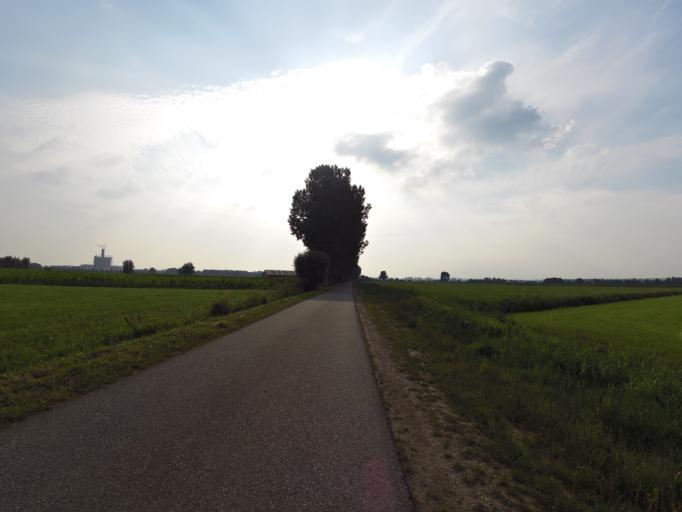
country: NL
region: Gelderland
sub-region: Gemeente Rheden
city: Rheden
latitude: 51.9784
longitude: 6.0183
